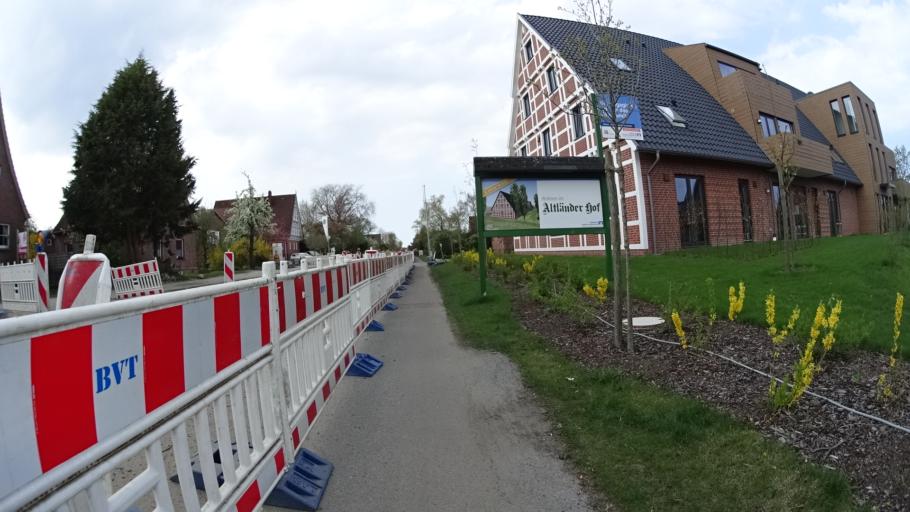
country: DE
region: Lower Saxony
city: Jork
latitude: 53.5259
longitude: 9.7072
